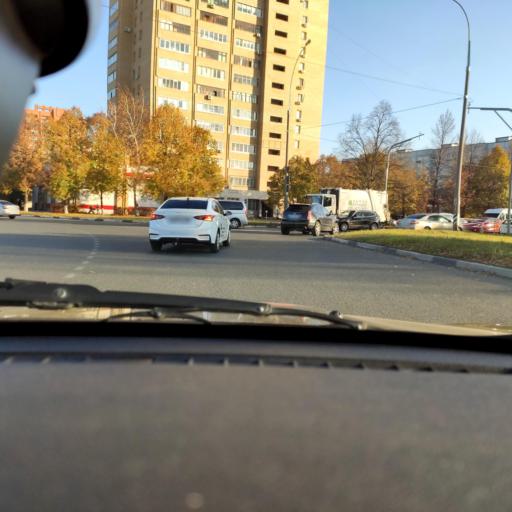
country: RU
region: Samara
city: Tol'yatti
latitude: 53.5259
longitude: 49.3113
